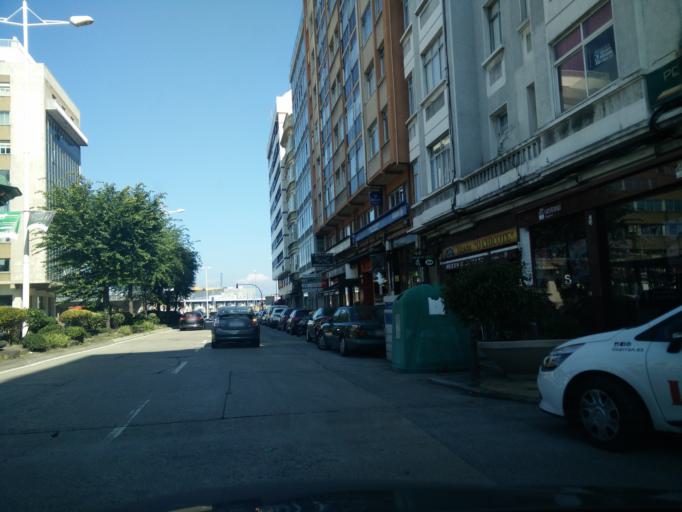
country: ES
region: Galicia
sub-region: Provincia da Coruna
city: A Coruna
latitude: 43.3569
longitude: -8.4008
